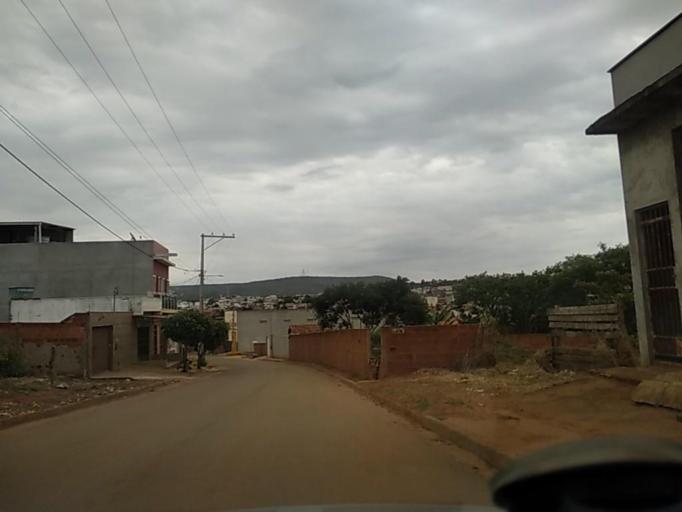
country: BR
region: Bahia
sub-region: Caetite
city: Caetite
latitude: -14.0518
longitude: -42.4759
